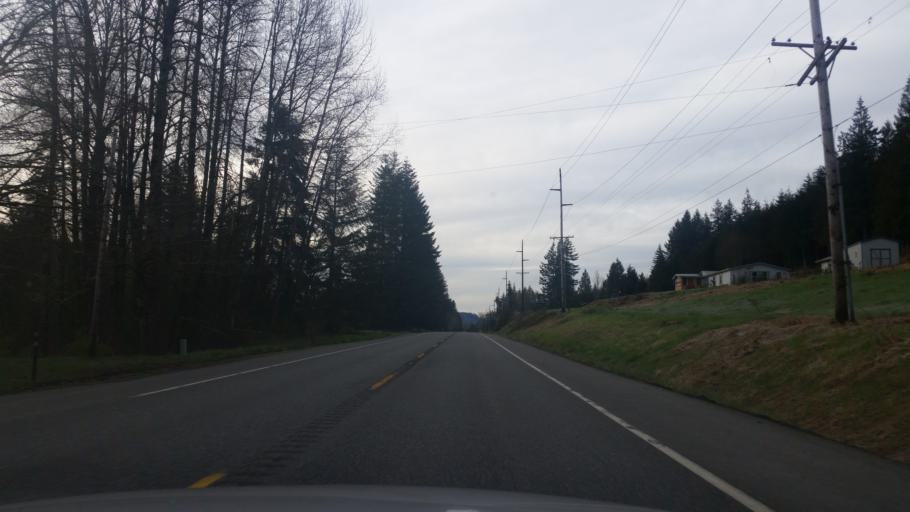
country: US
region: Washington
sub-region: Pierce County
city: Eatonville
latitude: 46.7920
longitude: -122.2658
